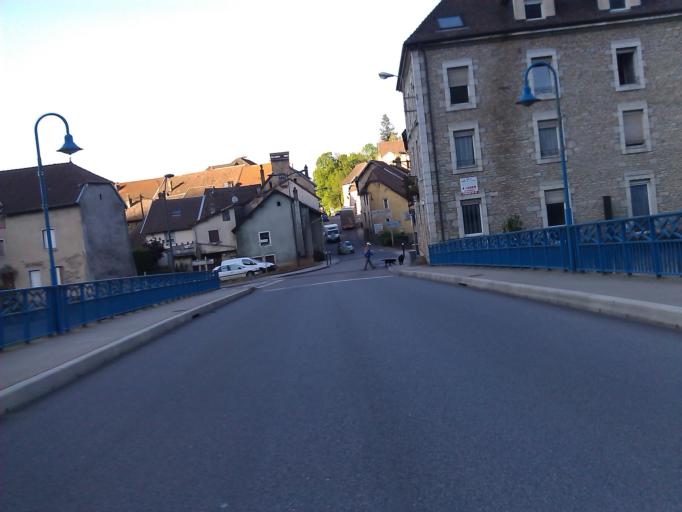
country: FR
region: Franche-Comte
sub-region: Departement du Doubs
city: Clerval
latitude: 47.3922
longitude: 6.4952
